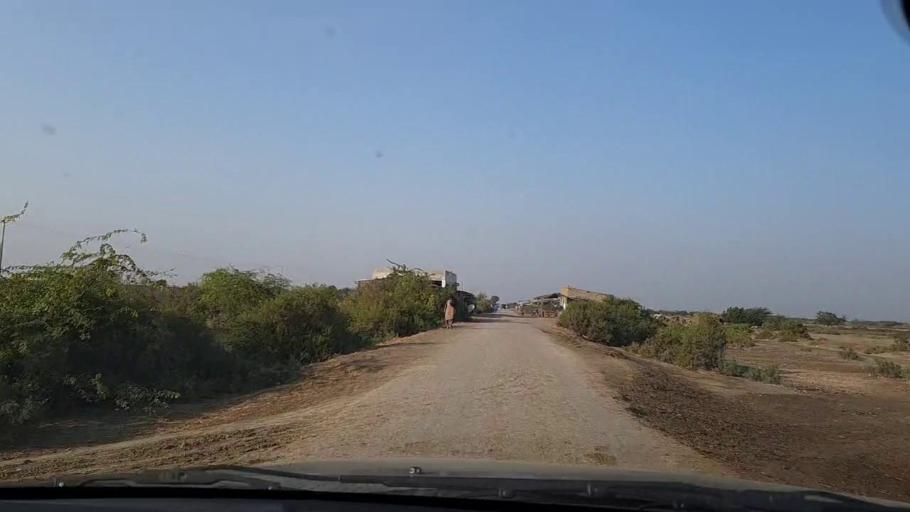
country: PK
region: Sindh
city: Chuhar Jamali
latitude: 24.3019
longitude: 67.7556
